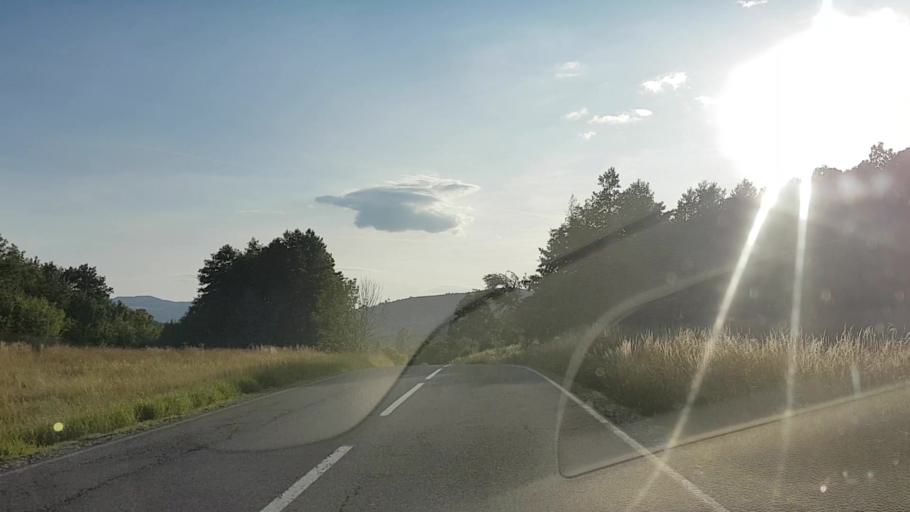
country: RO
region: Harghita
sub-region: Comuna Praid
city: Ocna de Sus
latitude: 46.5711
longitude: 25.1852
